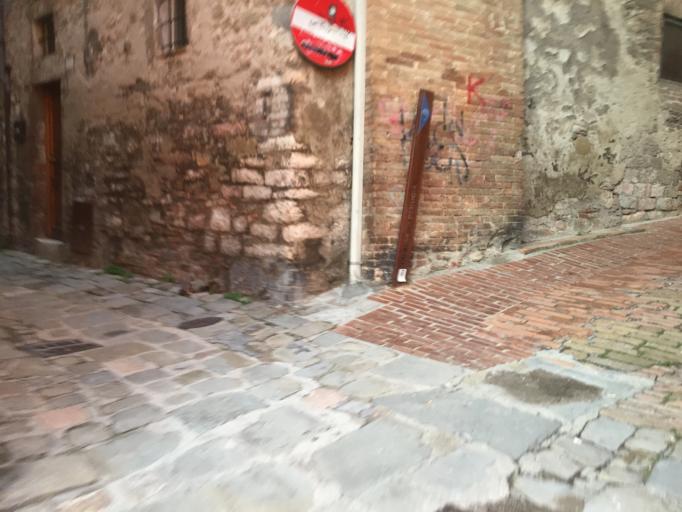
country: IT
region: Umbria
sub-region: Provincia di Perugia
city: Perugia
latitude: 43.1111
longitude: 12.3864
